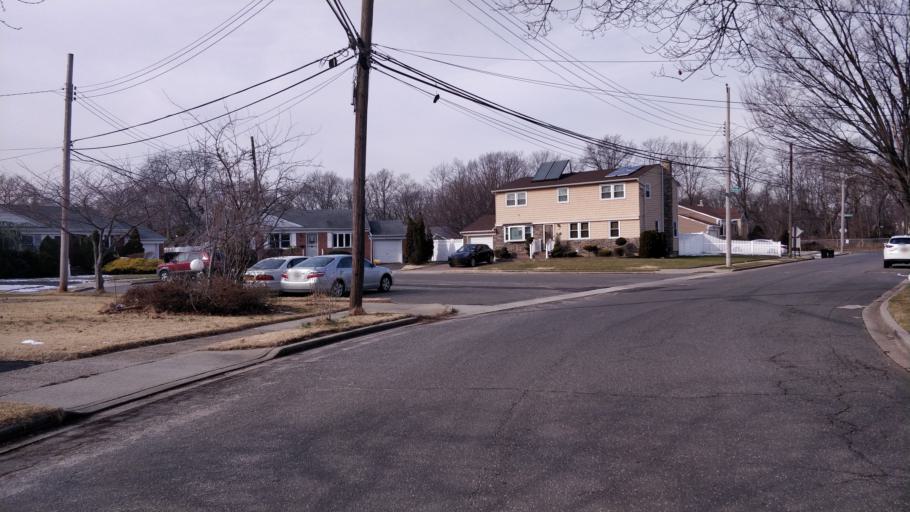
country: US
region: New York
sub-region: Nassau County
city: Jericho
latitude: 40.7787
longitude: -73.5368
